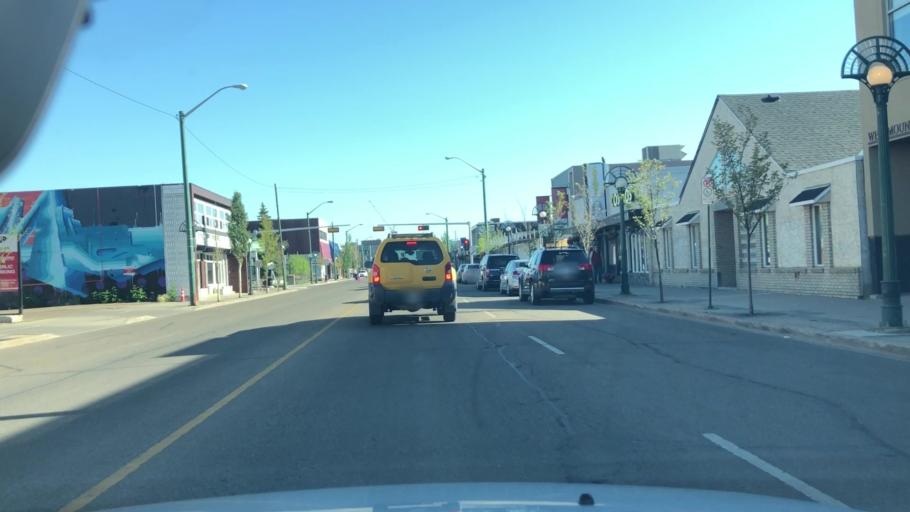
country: CA
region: Alberta
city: Edmonton
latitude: 53.5533
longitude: -113.5359
